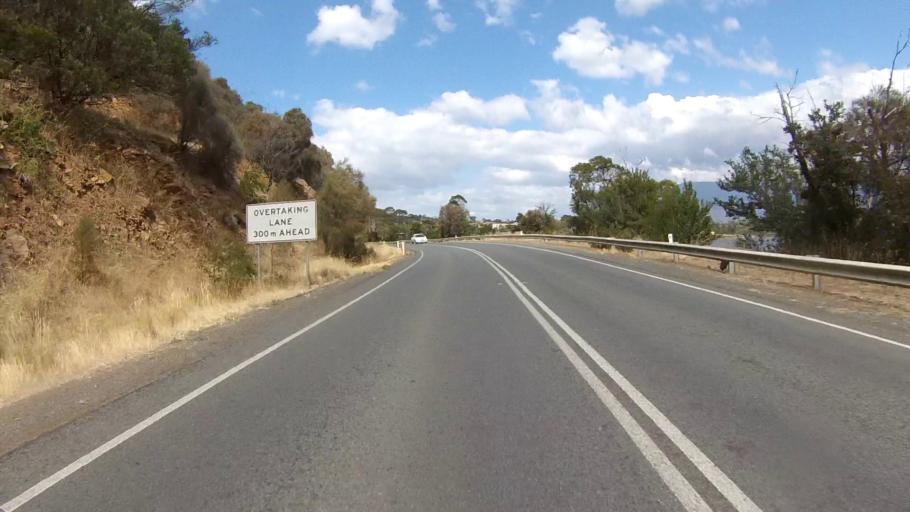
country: AU
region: Tasmania
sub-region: Brighton
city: Old Beach
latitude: -42.7867
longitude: 147.2912
